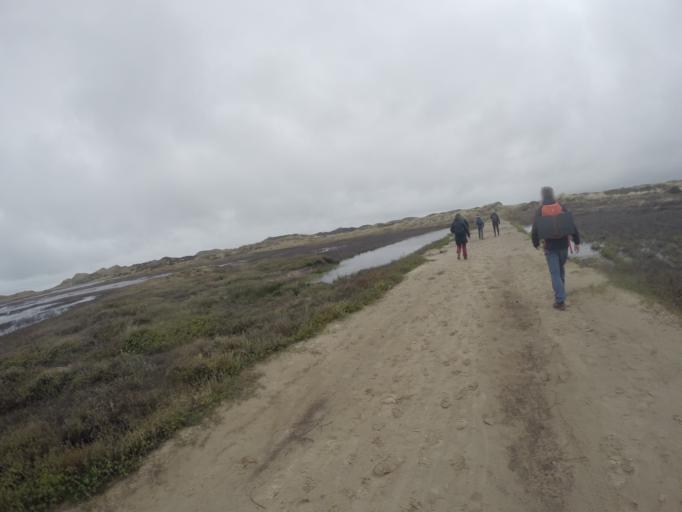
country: DK
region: Central Jutland
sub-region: Lemvig Kommune
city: Thyboron
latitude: 56.8429
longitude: 8.2780
